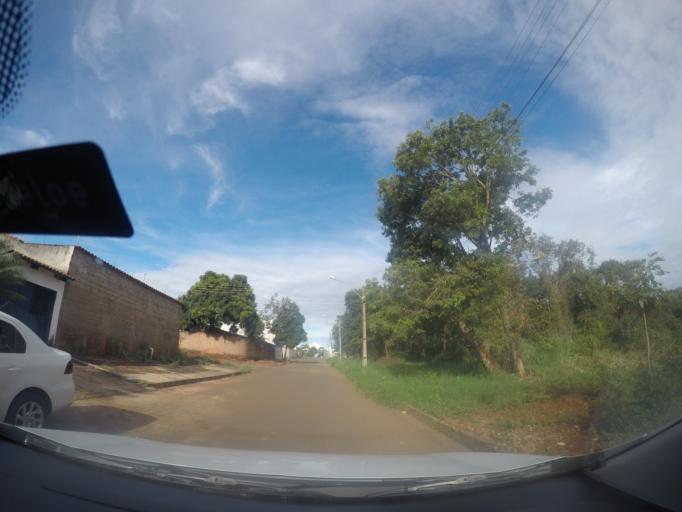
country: BR
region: Goias
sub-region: Goiania
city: Goiania
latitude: -16.6333
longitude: -49.3615
